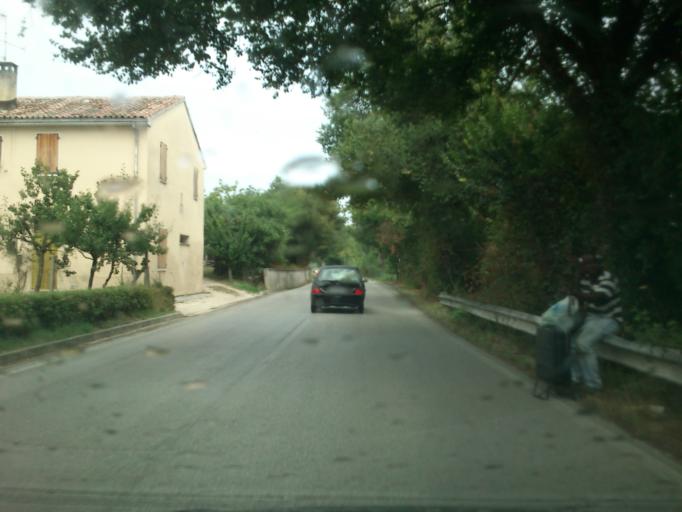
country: IT
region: The Marches
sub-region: Provincia di Pesaro e Urbino
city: Lucrezia
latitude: 43.7646
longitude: 12.9291
